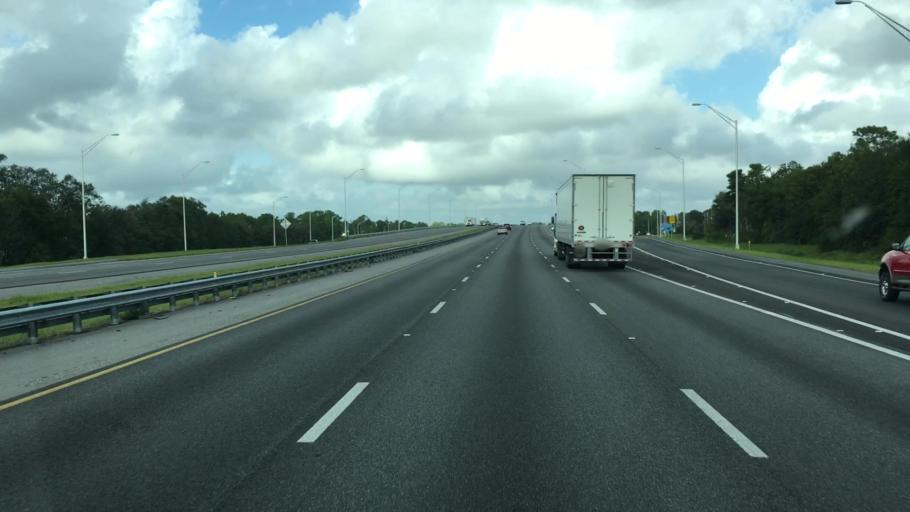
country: US
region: Florida
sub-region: Volusia County
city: Port Orange
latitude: 29.1015
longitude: -81.0263
